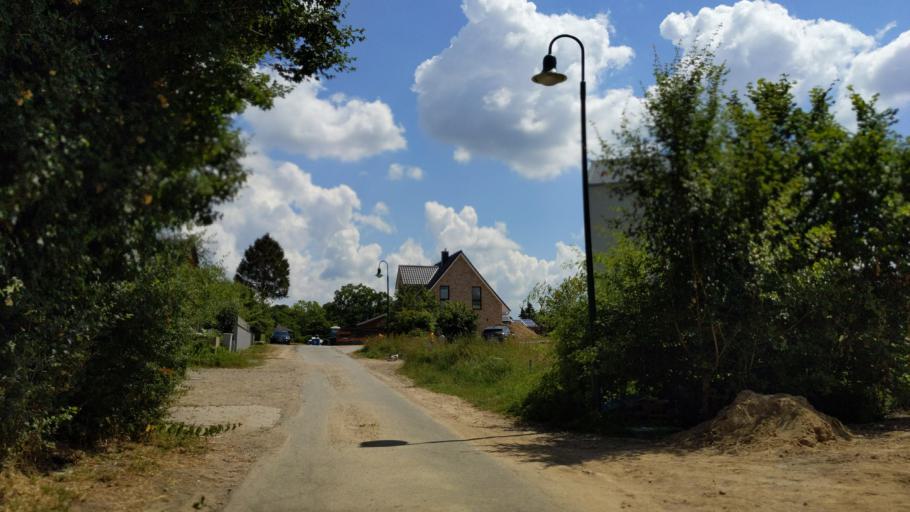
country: DE
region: Schleswig-Holstein
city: Bad Schwartau
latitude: 53.9417
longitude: 10.6536
